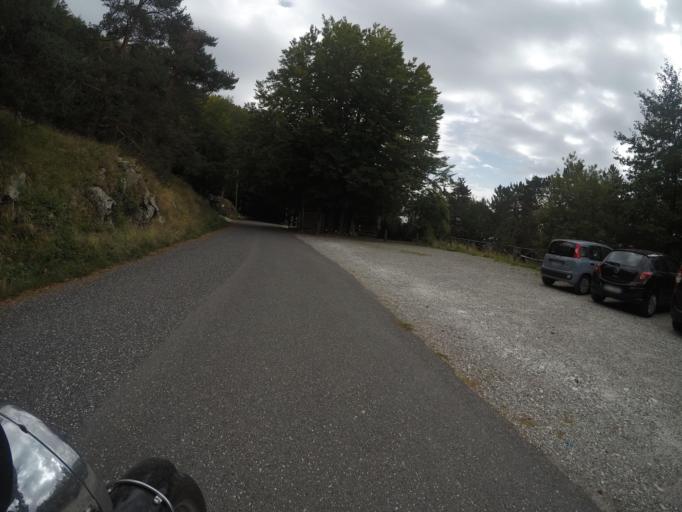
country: IT
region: Tuscany
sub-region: Provincia di Massa-Carrara
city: Carrara
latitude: 44.1203
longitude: 10.1216
